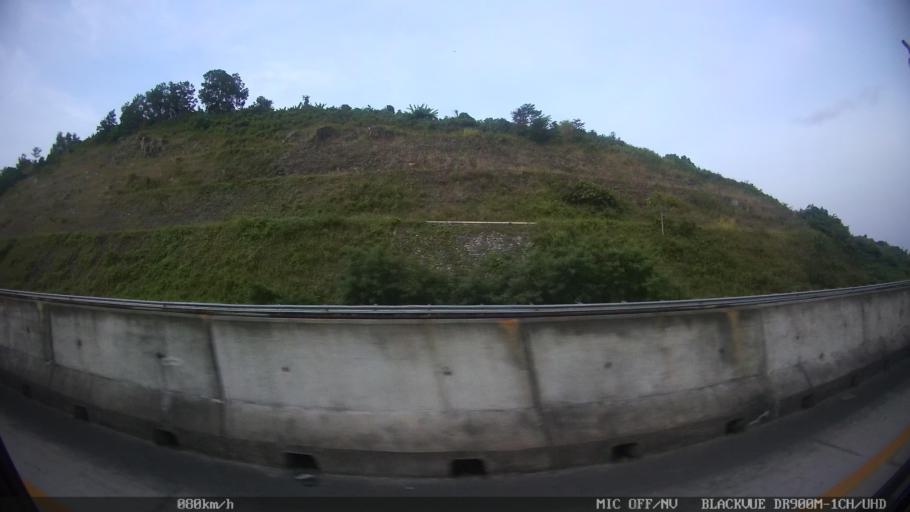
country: ID
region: Lampung
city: Penengahan
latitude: -5.8575
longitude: 105.7305
